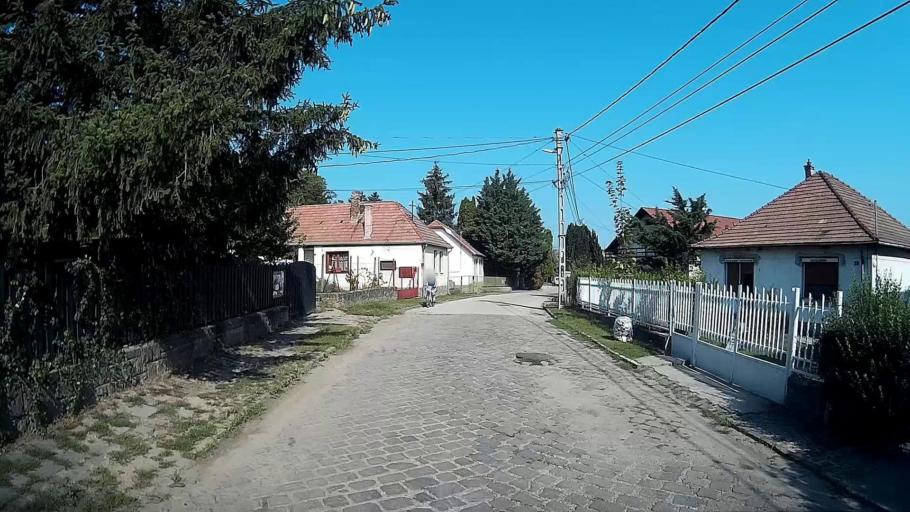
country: HU
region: Pest
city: Dunabogdany
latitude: 47.7900
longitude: 19.0365
